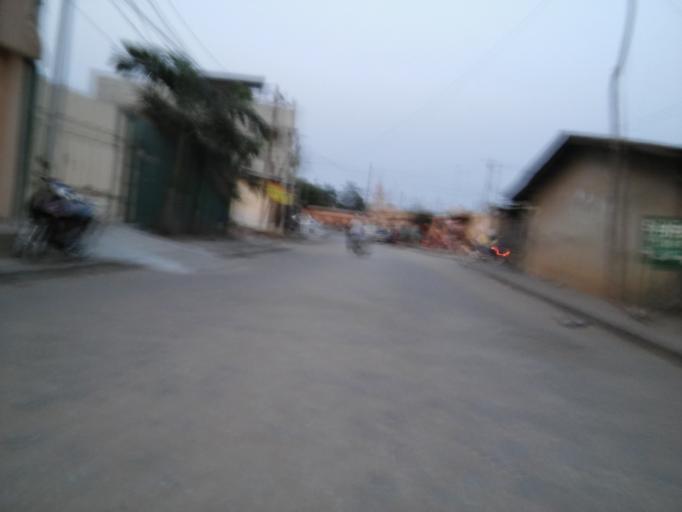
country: BJ
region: Atlantique
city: Abomey-Calavi
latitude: 6.3909
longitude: 2.3498
